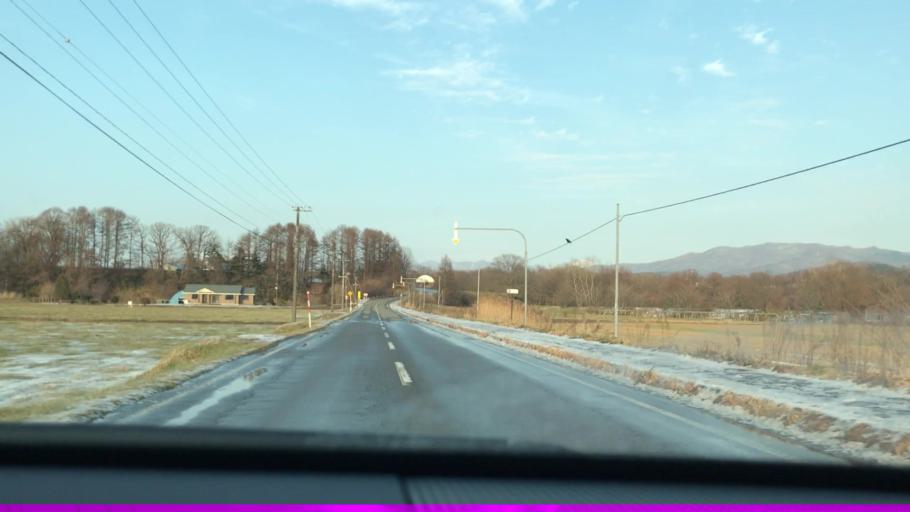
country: JP
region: Hokkaido
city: Shizunai-furukawacho
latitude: 42.4232
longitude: 142.4012
